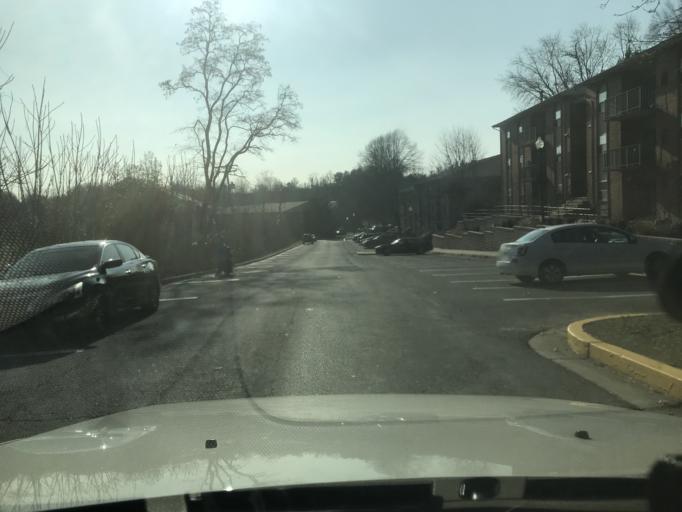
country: US
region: Maryland
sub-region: Baltimore County
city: Owings Mills
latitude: 39.4169
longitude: -76.7909
